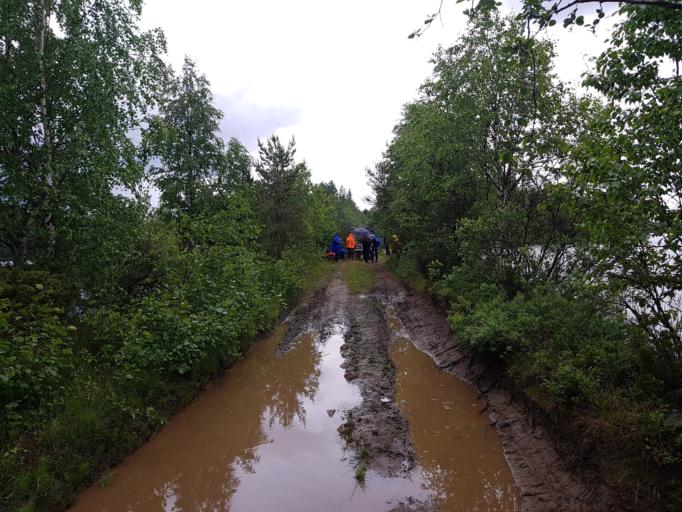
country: RU
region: Republic of Karelia
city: Kostomuksha
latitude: 64.8269
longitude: 29.8848
